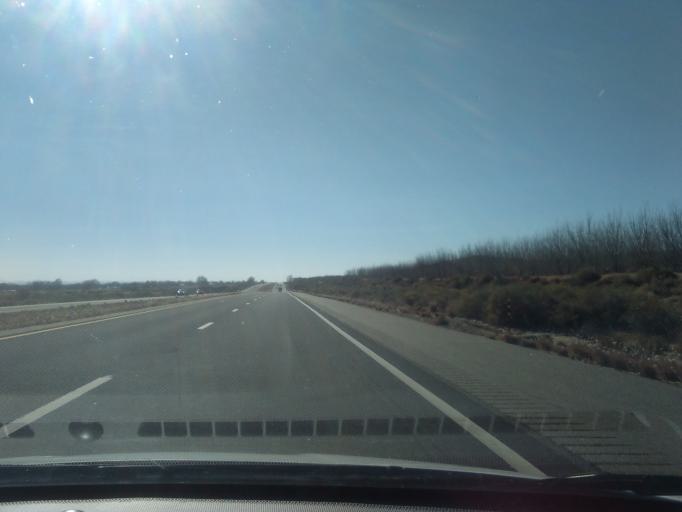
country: US
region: New Mexico
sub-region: Valencia County
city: Jarales
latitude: 34.5940
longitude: -106.7891
